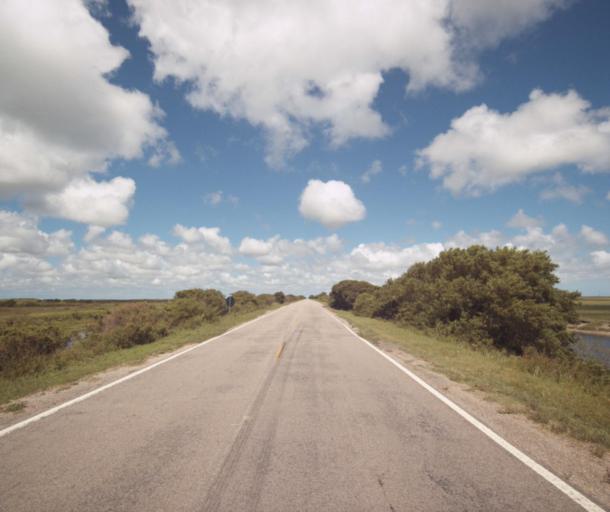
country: BR
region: Rio Grande do Sul
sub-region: Arroio Grande
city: Arroio Grande
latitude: -32.5435
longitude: -52.5416
